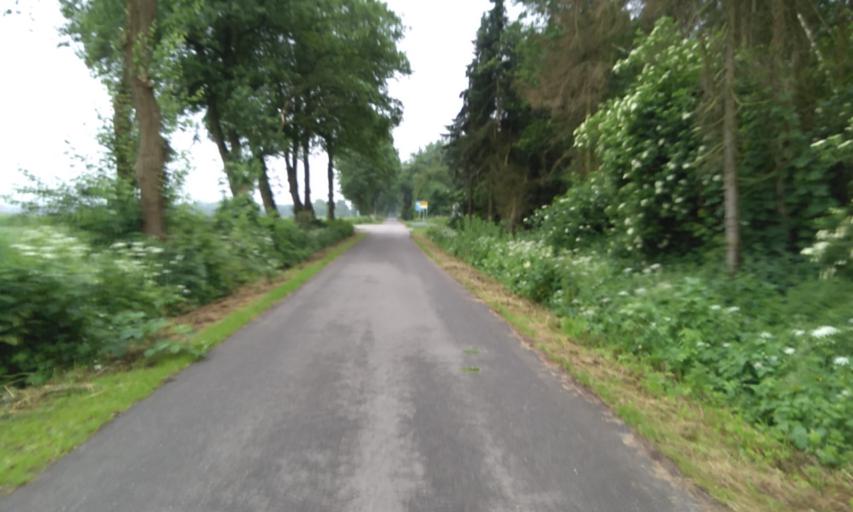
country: DE
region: Lower Saxony
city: Horneburg
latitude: 53.5187
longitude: 9.5726
